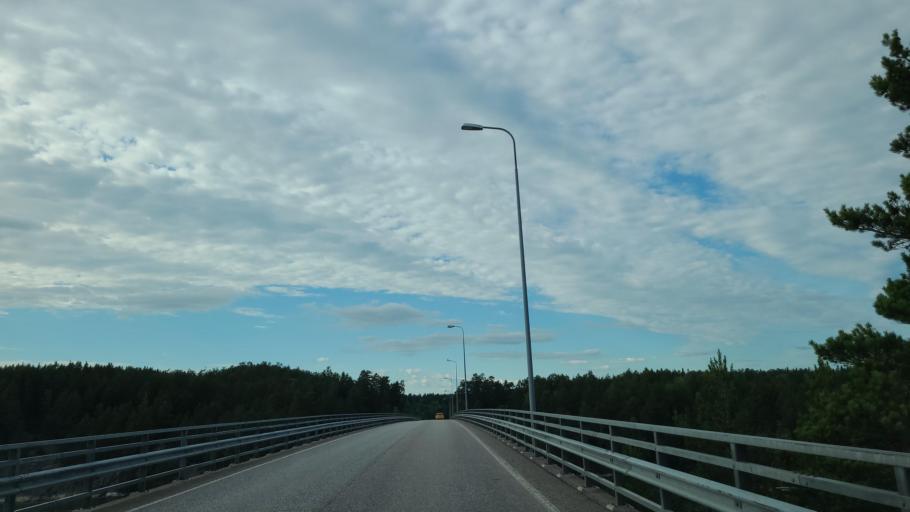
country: FI
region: Varsinais-Suomi
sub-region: Turku
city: Rymaettylae
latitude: 60.3359
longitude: 21.9799
